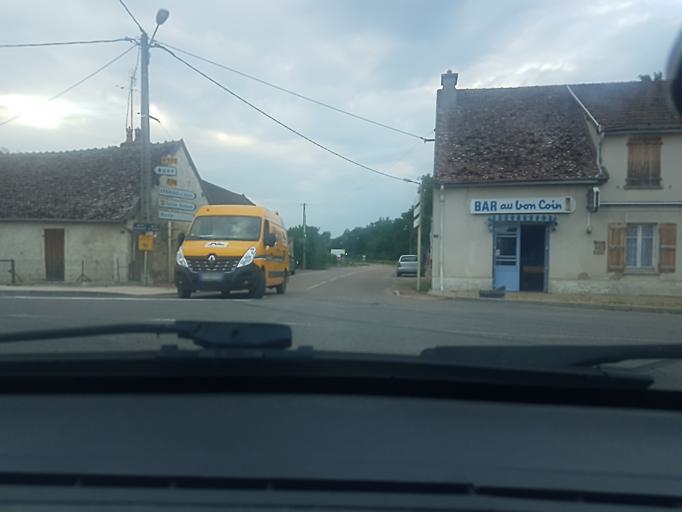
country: FR
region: Bourgogne
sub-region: Departement de Saone-et-Loire
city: Buxy
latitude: 46.7226
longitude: 4.7625
